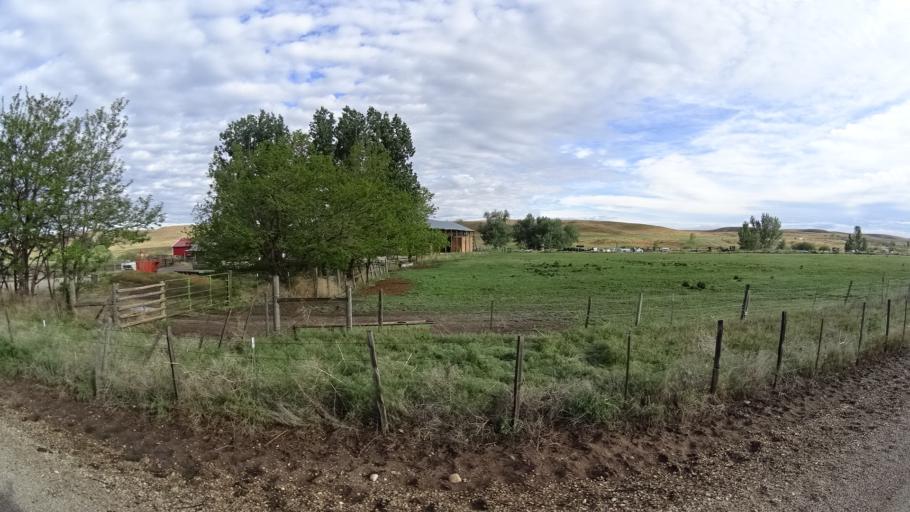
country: US
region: Idaho
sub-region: Ada County
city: Star
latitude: 43.7580
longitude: -116.5147
